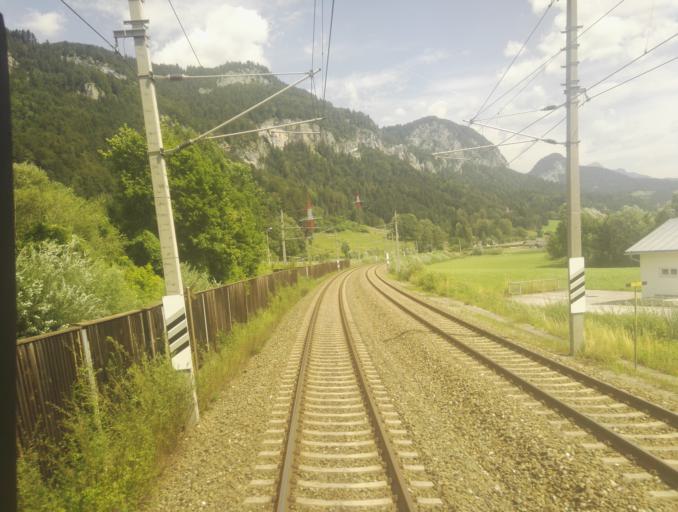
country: AT
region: Styria
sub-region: Politischer Bezirk Liezen
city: Stainach
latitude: 47.5390
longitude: 14.1190
